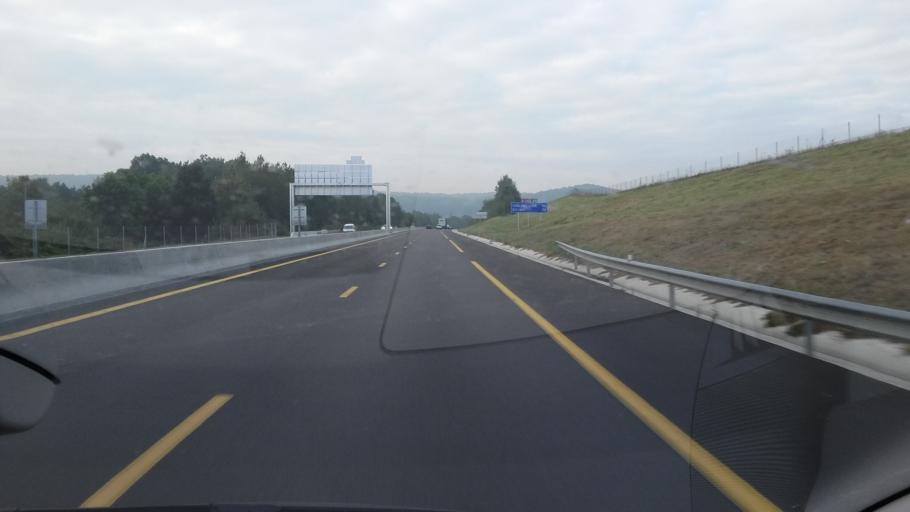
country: FR
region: Champagne-Ardenne
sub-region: Departement des Ardennes
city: La Francheville
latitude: 49.7081
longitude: 4.6990
